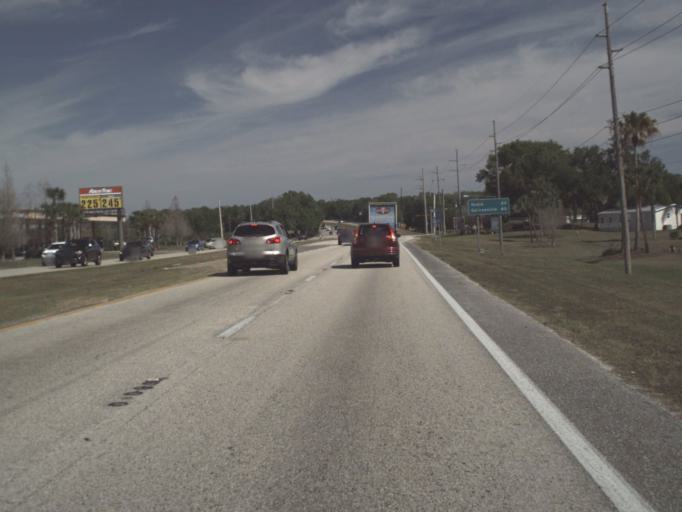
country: US
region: Florida
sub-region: Lake County
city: Lady Lake
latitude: 28.9216
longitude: -81.9242
